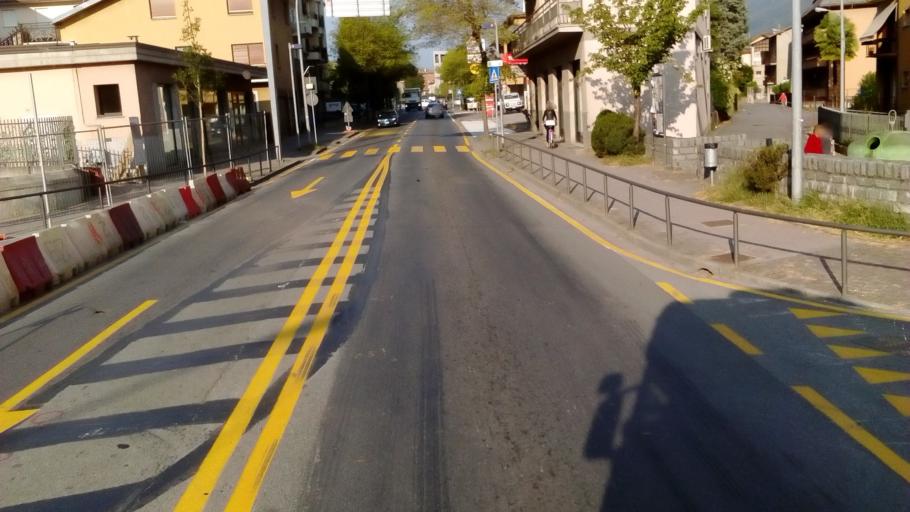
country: IT
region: Lombardy
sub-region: Provincia di Sondrio
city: Morbegno
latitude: 46.1350
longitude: 9.5746
